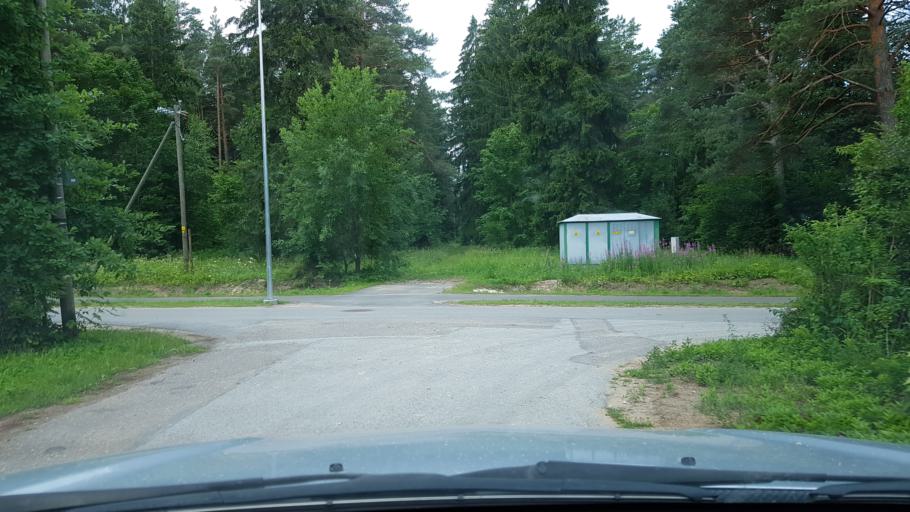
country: EE
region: Ida-Virumaa
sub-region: Narva-Joesuu linn
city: Narva-Joesuu
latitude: 59.4455
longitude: 28.0223
